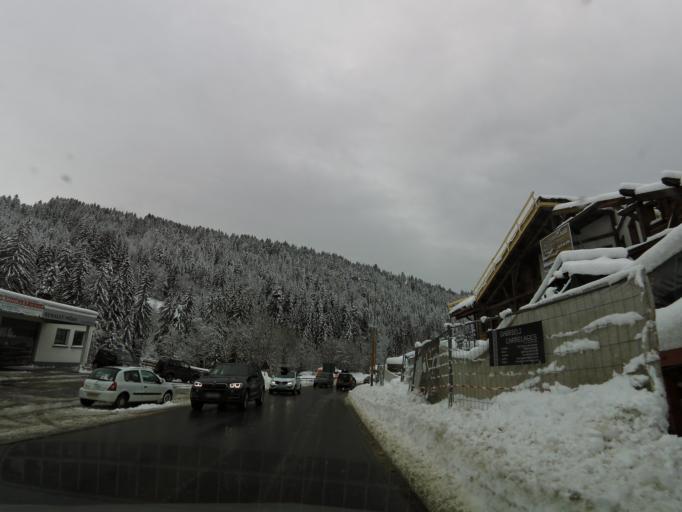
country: FR
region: Rhone-Alpes
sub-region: Departement de la Haute-Savoie
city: Les Gets
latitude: 46.1487
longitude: 6.6561
